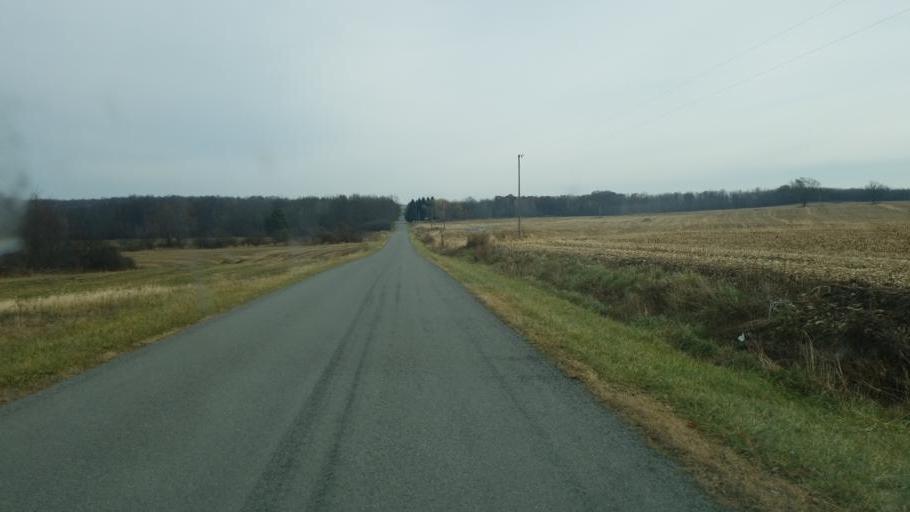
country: US
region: Pennsylvania
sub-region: Crawford County
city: Cochranton
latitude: 41.5011
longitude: -80.1082
